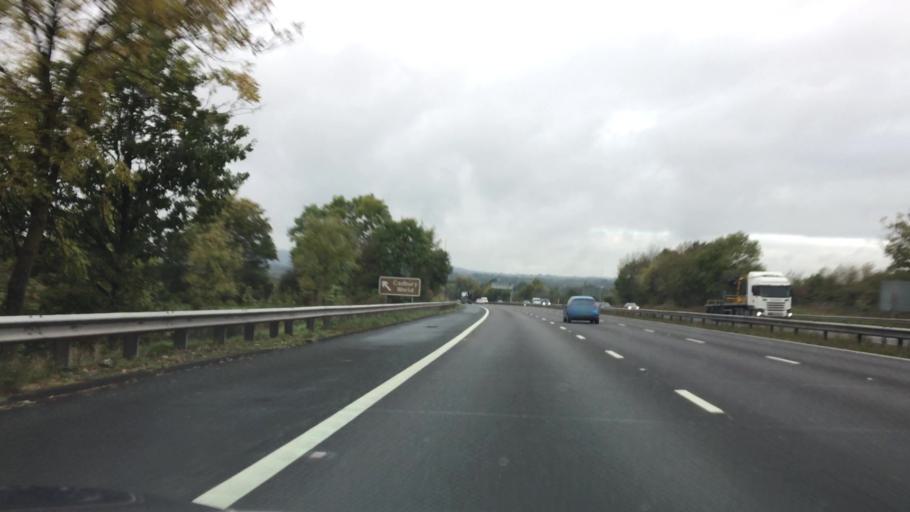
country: GB
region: England
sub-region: Worcestershire
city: Alvechurch
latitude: 52.3584
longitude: -1.9310
